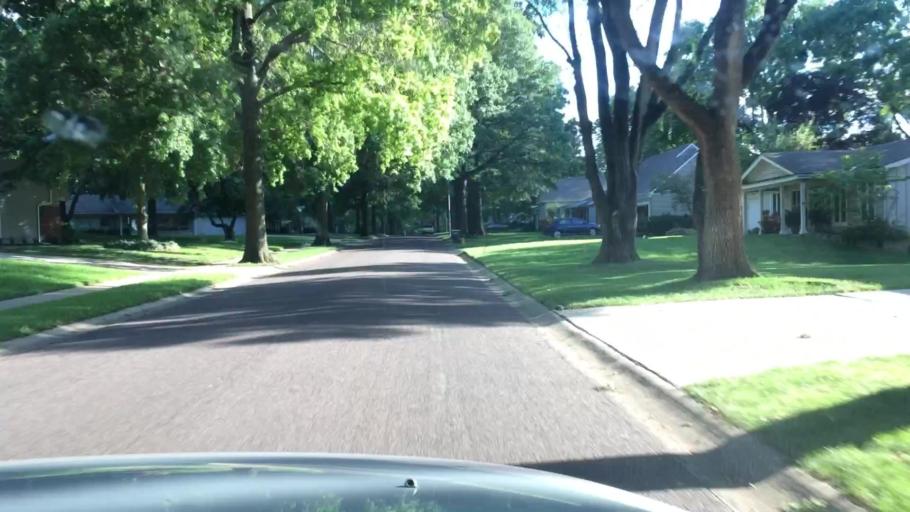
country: US
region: Kansas
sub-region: Johnson County
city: Overland Park
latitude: 38.9695
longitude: -94.6573
